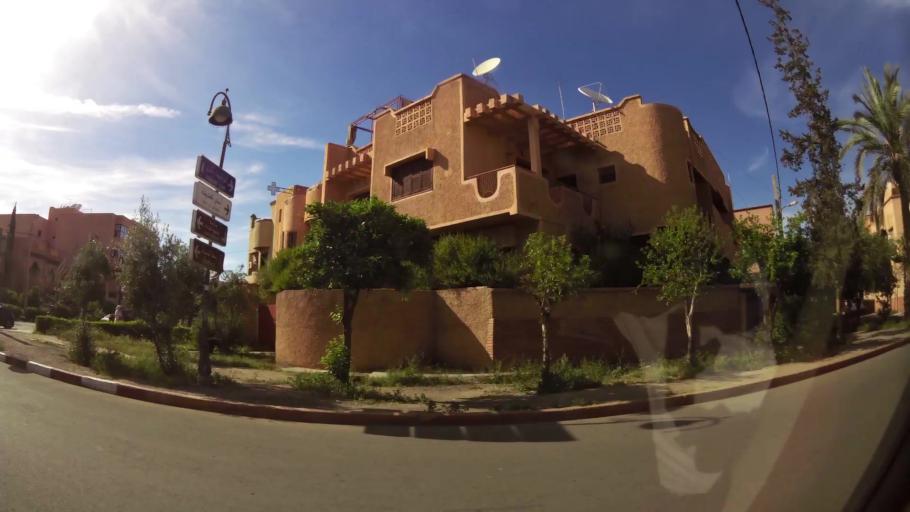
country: MA
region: Marrakech-Tensift-Al Haouz
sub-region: Marrakech
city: Marrakesh
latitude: 31.6535
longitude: -8.0084
